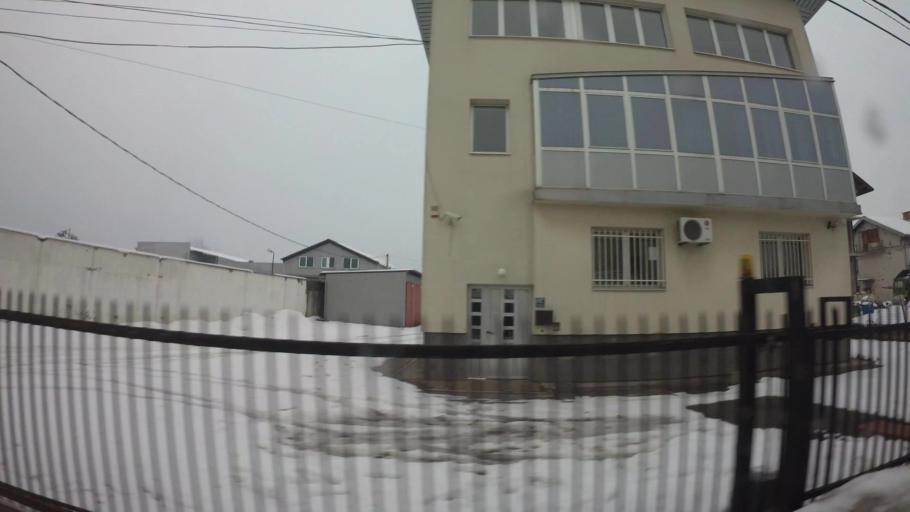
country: BA
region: Federation of Bosnia and Herzegovina
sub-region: Kanton Sarajevo
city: Sarajevo
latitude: 43.8453
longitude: 18.3166
